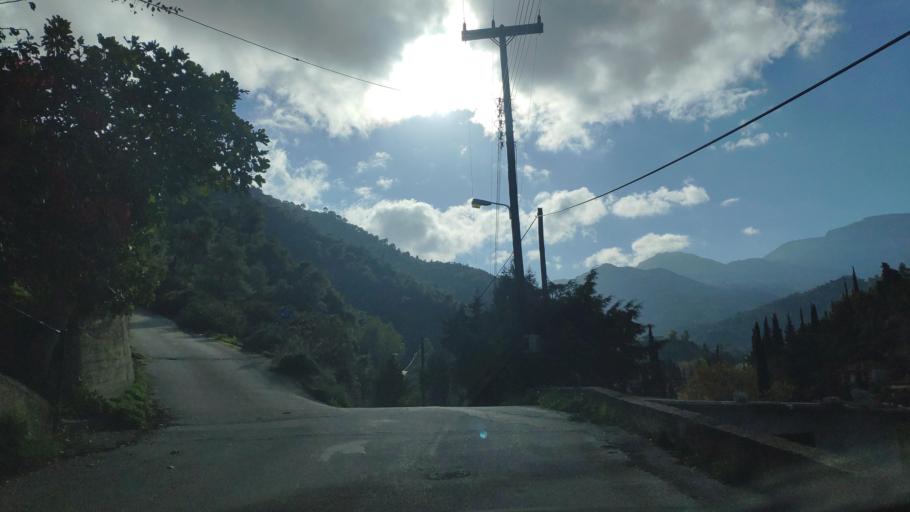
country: GR
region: West Greece
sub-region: Nomos Achaias
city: Aiyira
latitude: 38.1288
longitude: 22.4335
